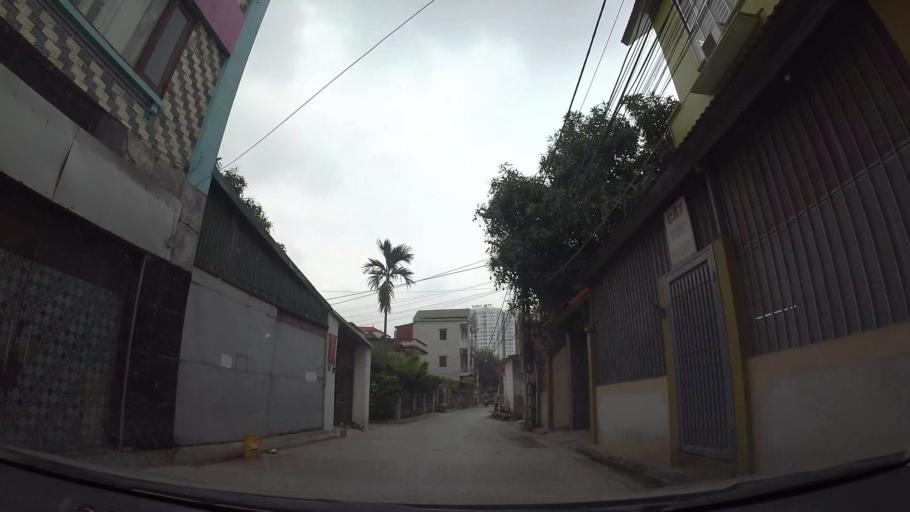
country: VN
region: Ha Noi
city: Trau Quy
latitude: 21.0384
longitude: 105.9357
